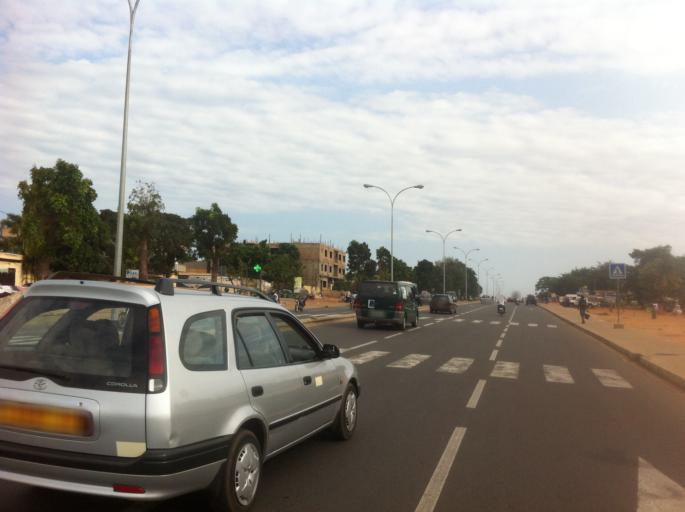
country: TG
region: Maritime
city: Lome
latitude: 6.1579
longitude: 1.2016
